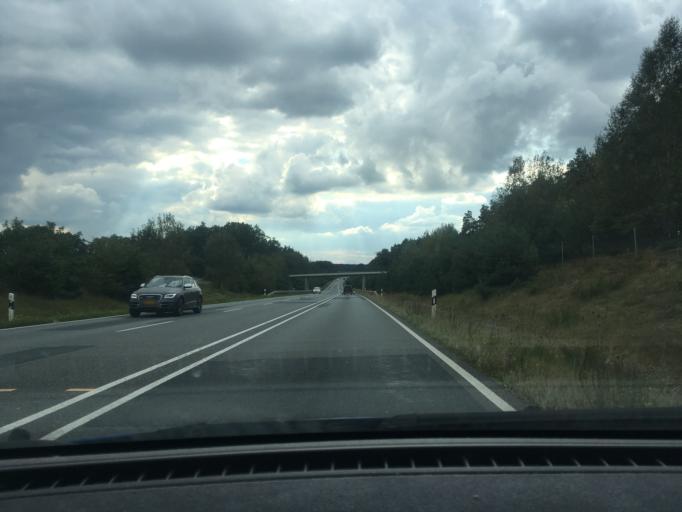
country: DE
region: Lower Saxony
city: Uelzen
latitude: 52.9414
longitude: 10.5714
